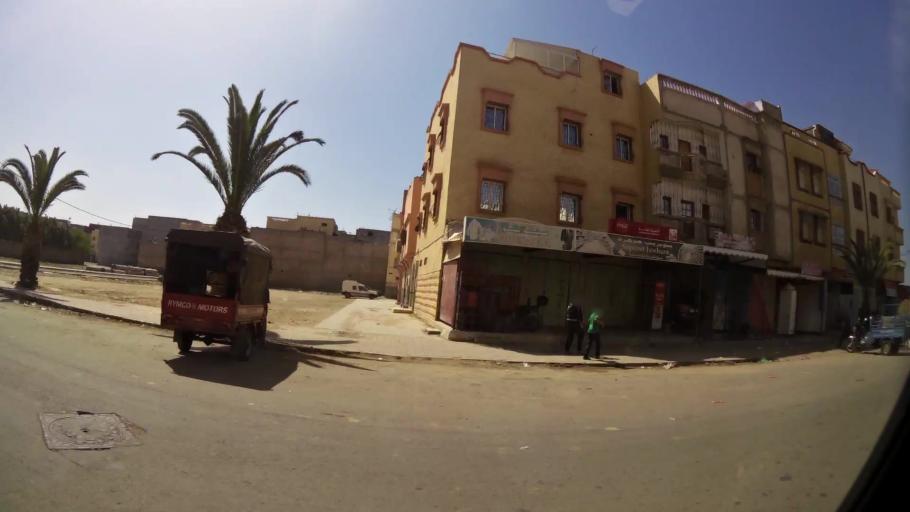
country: MA
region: Souss-Massa-Draa
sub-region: Inezgane-Ait Mellou
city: Inezgane
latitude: 30.3511
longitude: -9.5563
